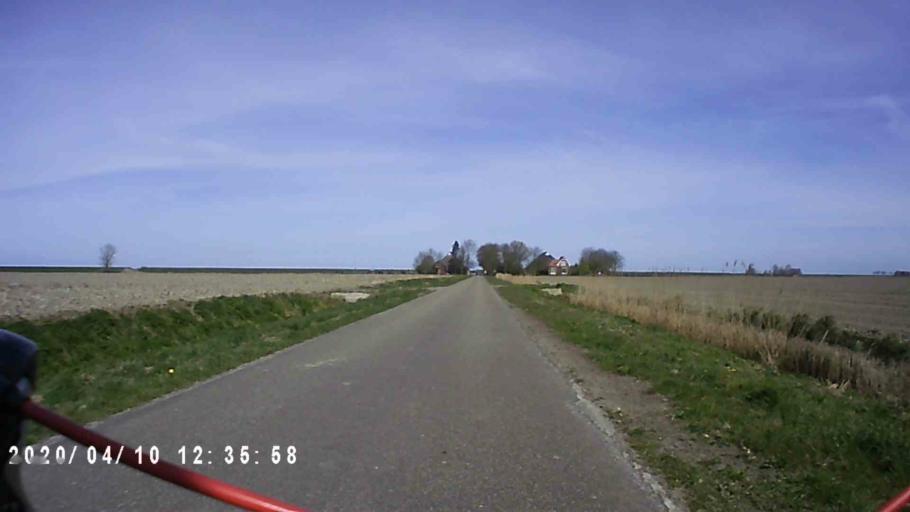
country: NL
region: Groningen
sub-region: Gemeente De Marne
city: Ulrum
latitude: 53.4017
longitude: 6.4176
